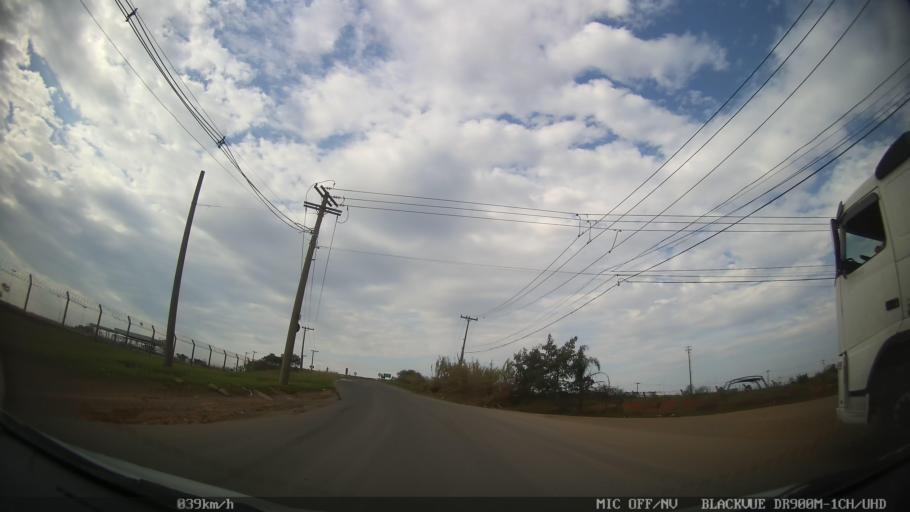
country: BR
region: Sao Paulo
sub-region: Paulinia
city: Paulinia
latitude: -22.7120
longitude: -47.1448
